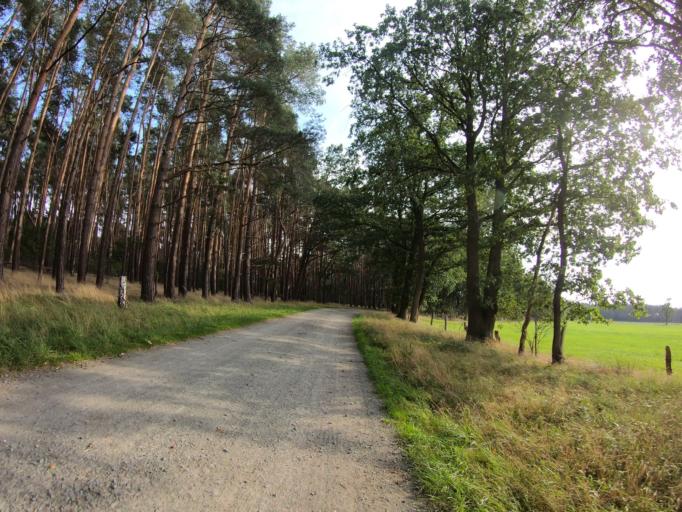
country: DE
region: Lower Saxony
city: Ribbesbuttel
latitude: 52.4494
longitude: 10.5243
